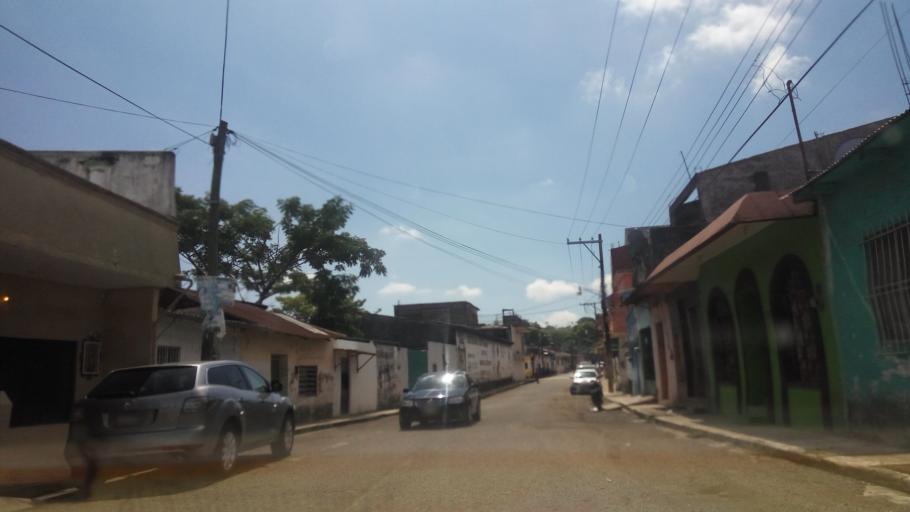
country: MX
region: Tabasco
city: Teapa
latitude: 17.5473
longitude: -92.9512
